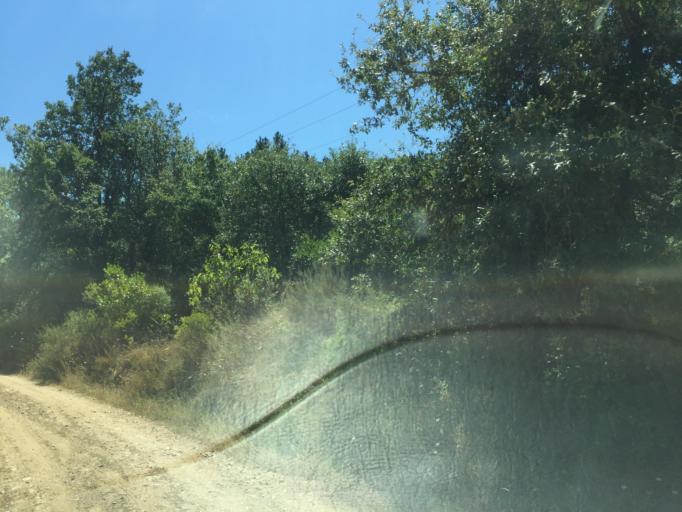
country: PT
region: Santarem
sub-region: Tomar
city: Tomar
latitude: 39.5974
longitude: -8.3570
